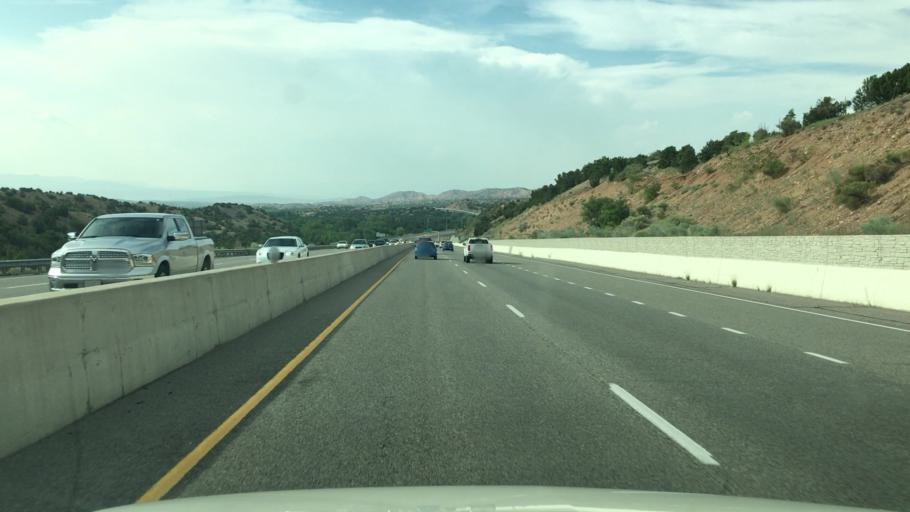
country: US
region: New Mexico
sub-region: Santa Fe County
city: Santa Fe
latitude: 35.7739
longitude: -105.9452
